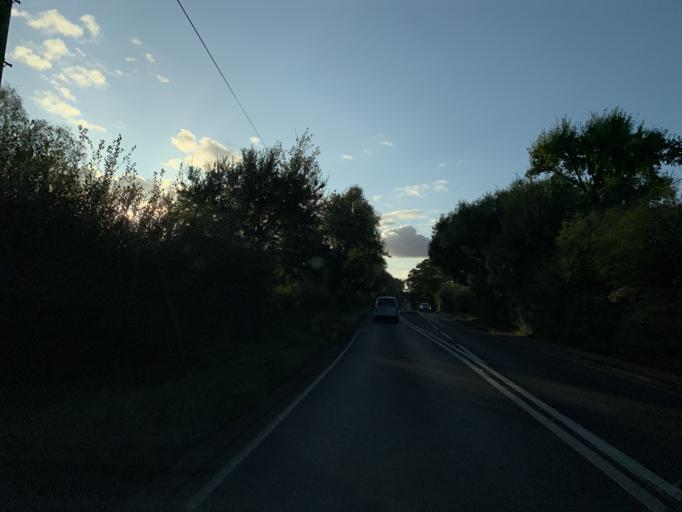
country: GB
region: England
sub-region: Hampshire
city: West Wellow
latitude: 50.9713
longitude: -1.5946
